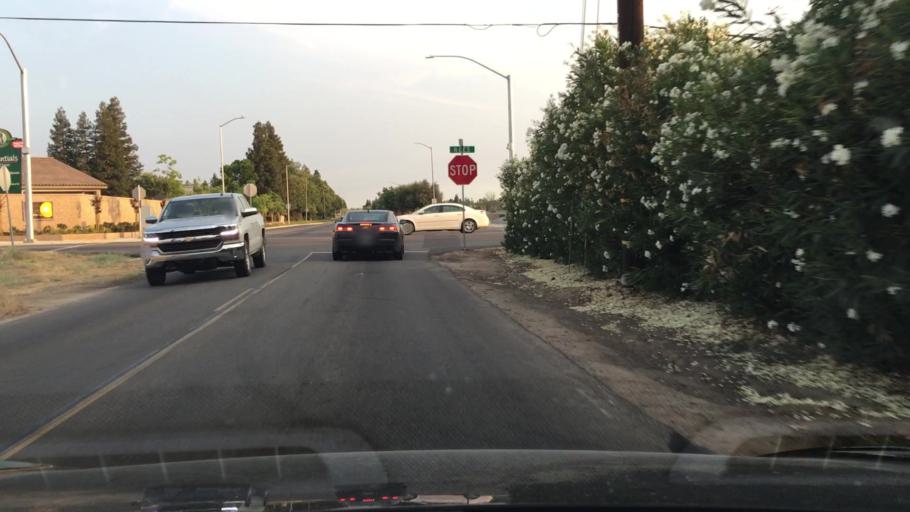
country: US
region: California
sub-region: Fresno County
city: Clovis
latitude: 36.8523
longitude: -119.6931
